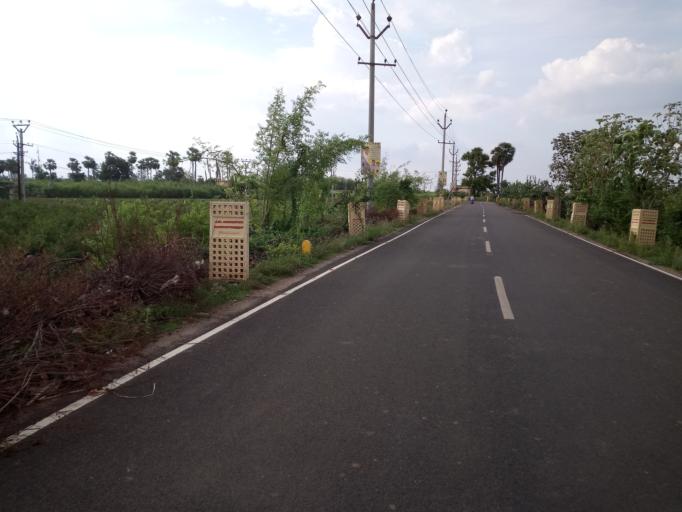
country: IN
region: Andhra Pradesh
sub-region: Guntur
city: Tadepalle
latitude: 16.5013
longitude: 80.5818
